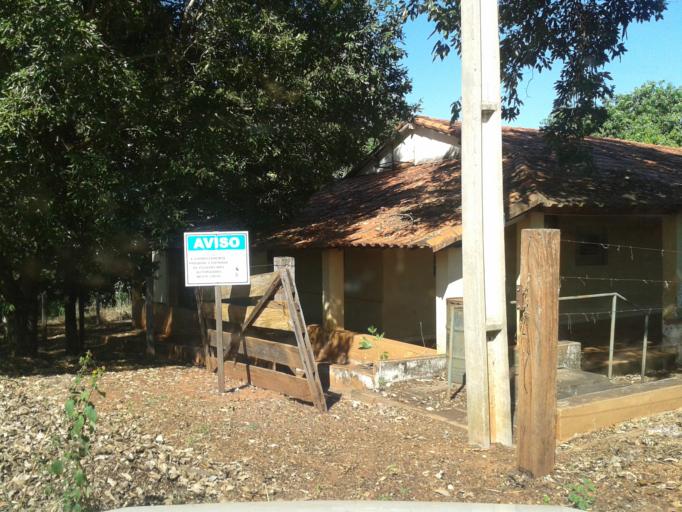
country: BR
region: Minas Gerais
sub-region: Santa Vitoria
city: Santa Vitoria
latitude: -19.0603
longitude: -50.3830
